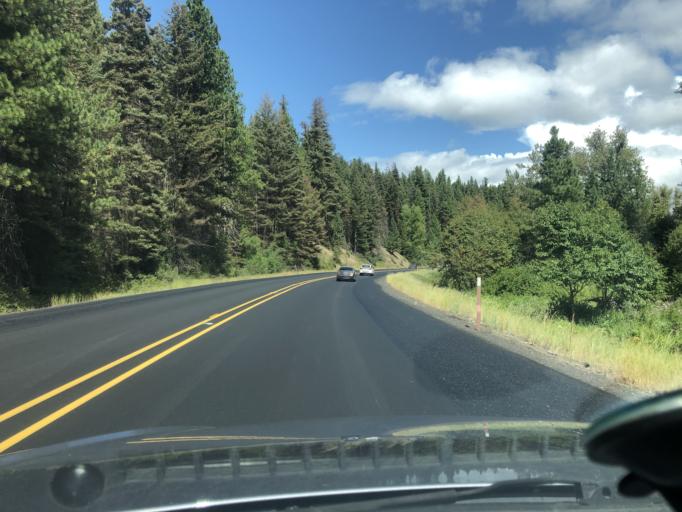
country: US
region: Washington
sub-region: Kittitas County
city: Cle Elum
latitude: 47.2980
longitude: -120.7010
